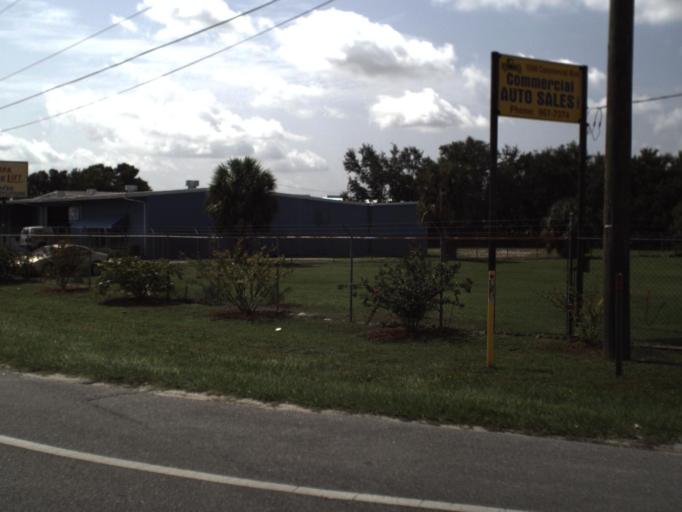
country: US
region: Florida
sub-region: Polk County
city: Inwood
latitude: 28.0394
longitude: -81.7849
